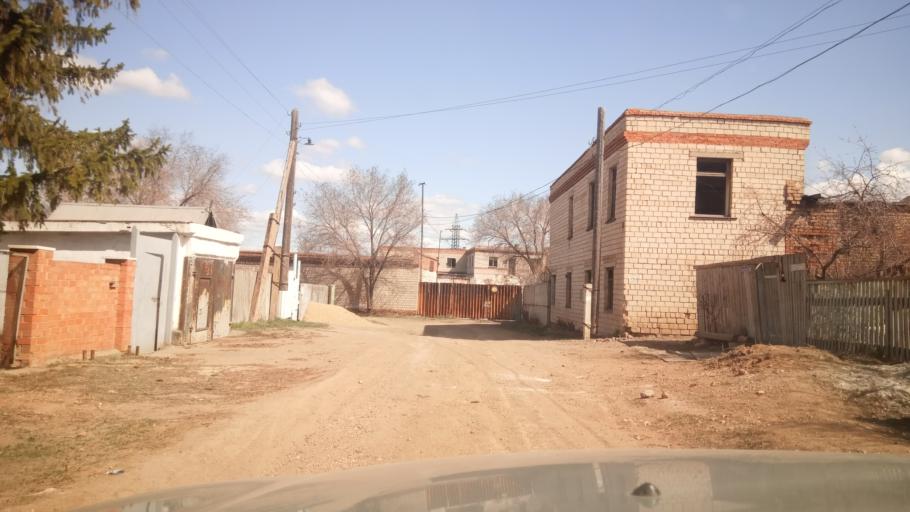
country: RU
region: Orenburg
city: Novotroitsk
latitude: 51.2096
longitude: 58.3172
